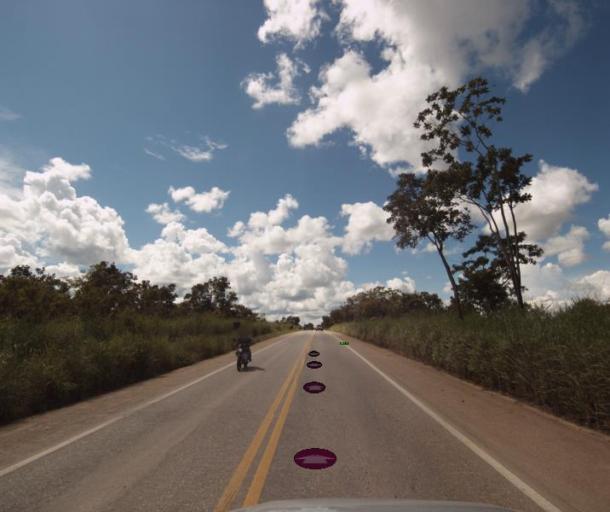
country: BR
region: Goias
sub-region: Porangatu
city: Porangatu
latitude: -13.5939
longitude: -49.0418
